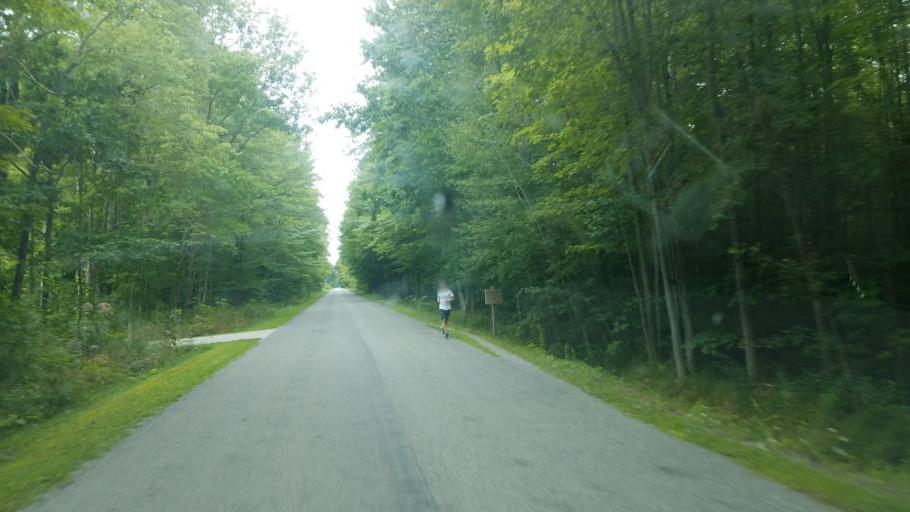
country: US
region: Pennsylvania
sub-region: Erie County
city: Lake City
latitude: 41.9939
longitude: -80.4401
